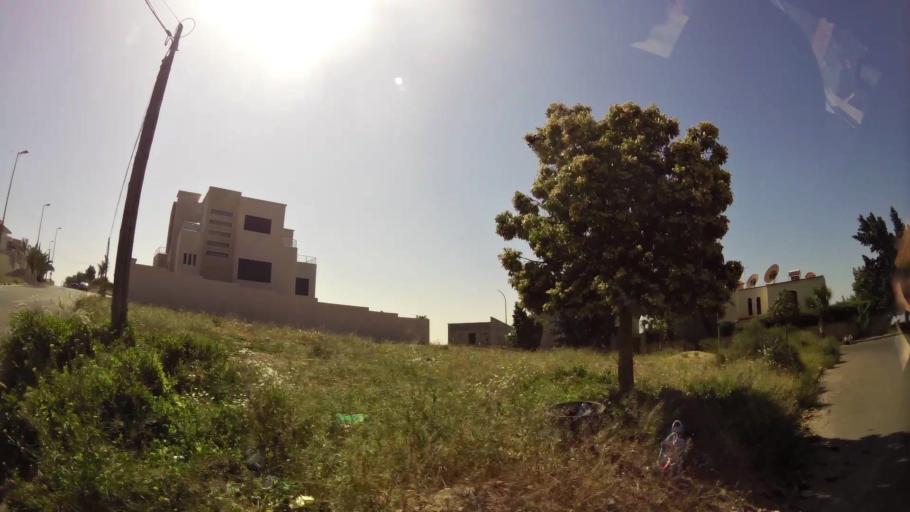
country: MA
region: Souss-Massa-Draa
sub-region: Agadir-Ida-ou-Tnan
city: Agadir
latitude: 30.4438
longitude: -9.5838
